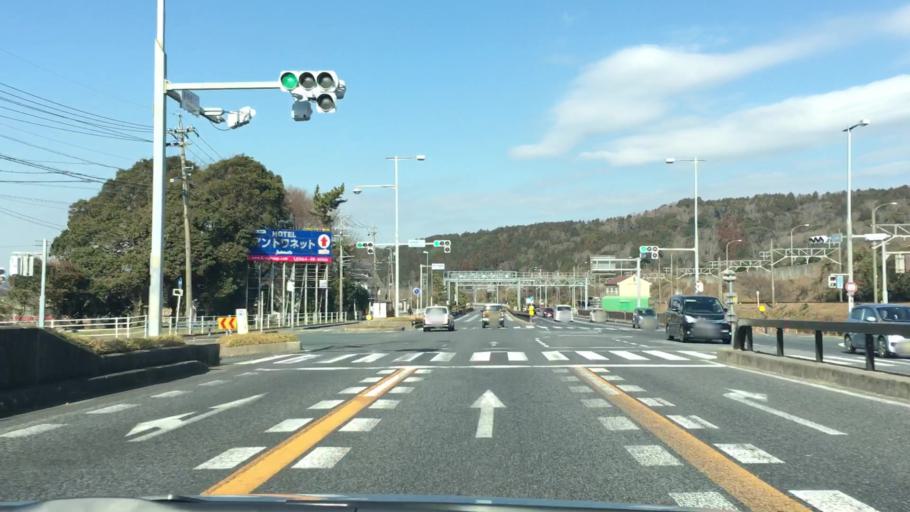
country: JP
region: Aichi
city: Gamagori
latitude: 34.8867
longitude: 137.2647
